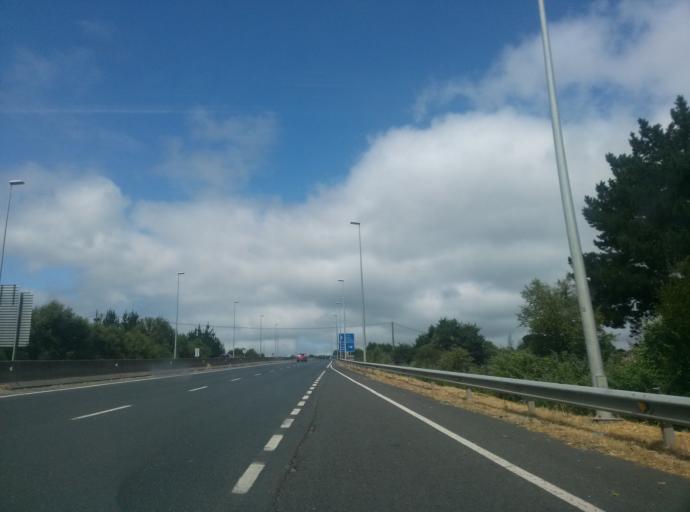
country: ES
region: Galicia
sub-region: Provincia de Lugo
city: Lugo
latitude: 43.0549
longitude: -7.5628
